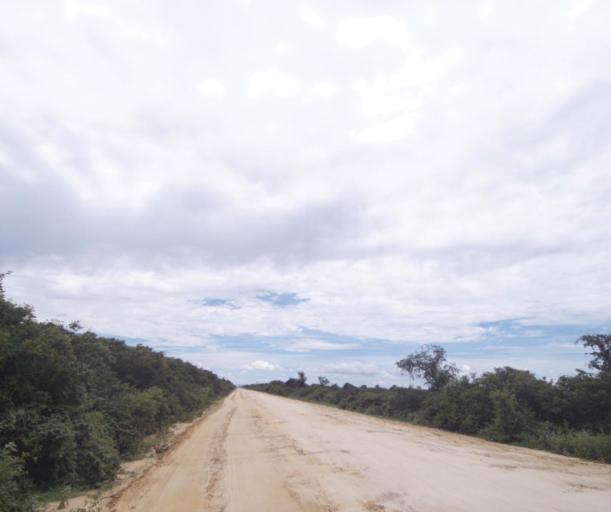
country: BR
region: Bahia
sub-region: Carinhanha
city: Carinhanha
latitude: -14.2413
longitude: -43.8497
